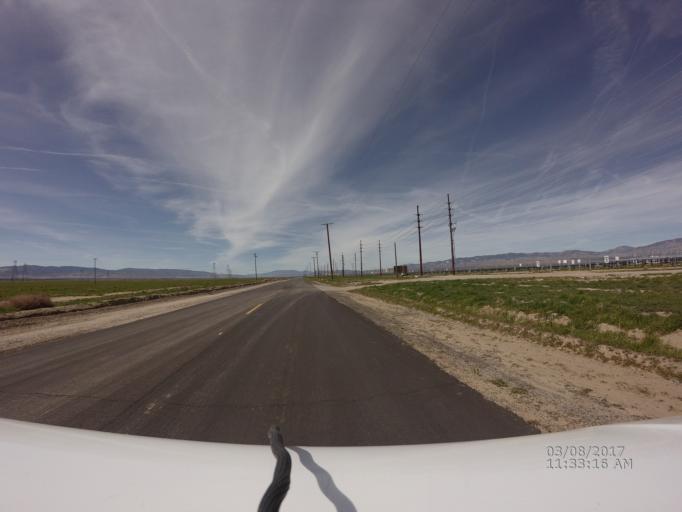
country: US
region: California
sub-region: Los Angeles County
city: Green Valley
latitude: 34.8191
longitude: -118.3997
